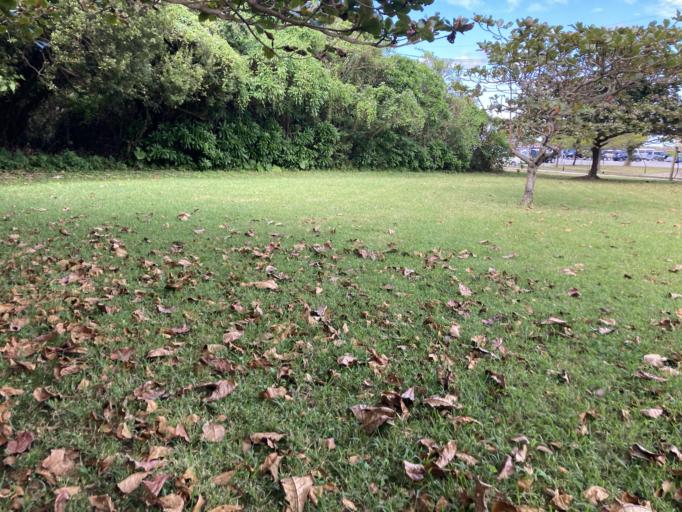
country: JP
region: Okinawa
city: Ishikawa
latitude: 26.4357
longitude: 127.7920
